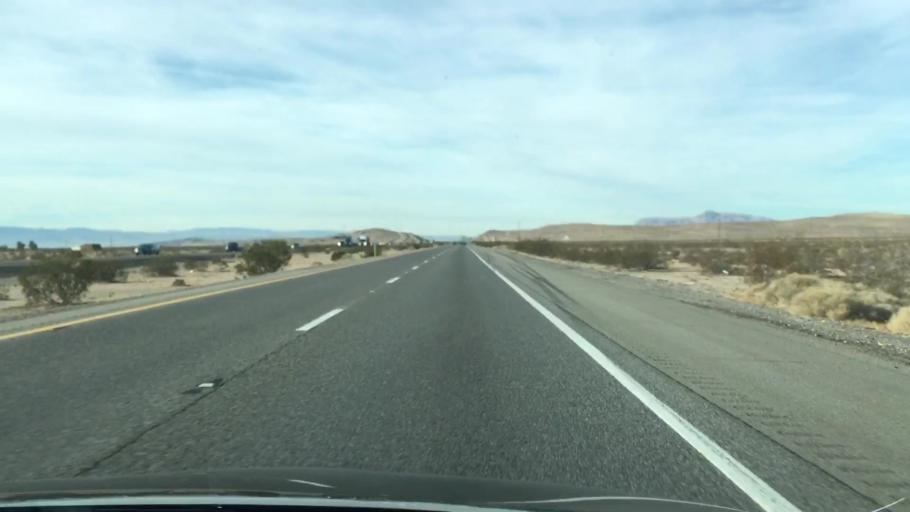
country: US
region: California
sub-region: San Bernardino County
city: Fort Irwin
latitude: 34.9777
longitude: -116.6131
